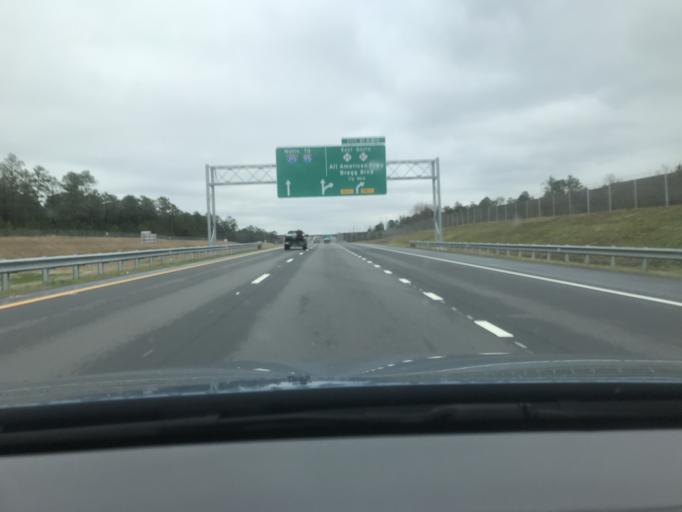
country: US
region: North Carolina
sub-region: Cumberland County
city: Fort Bragg
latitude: 35.1076
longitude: -78.9942
